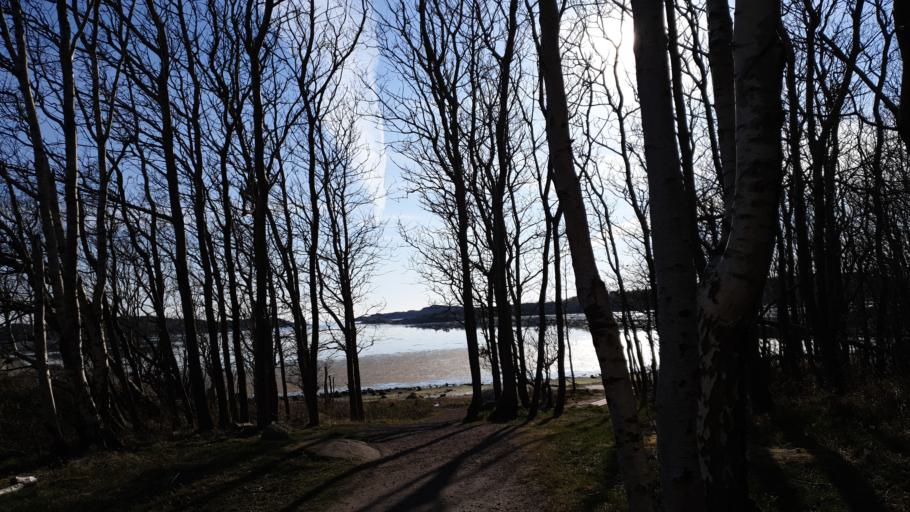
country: SE
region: Vaestra Goetaland
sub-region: Goteborg
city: Billdal
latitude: 57.5897
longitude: 11.9131
